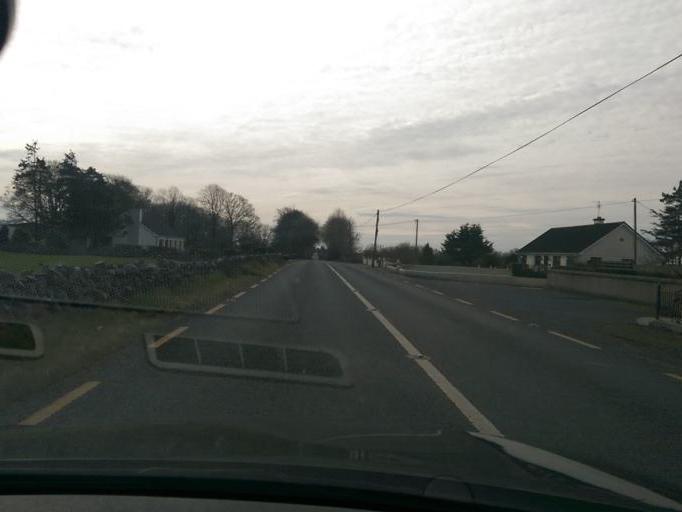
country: IE
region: Connaught
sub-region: County Galway
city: Claregalway
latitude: 53.3937
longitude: -8.8393
